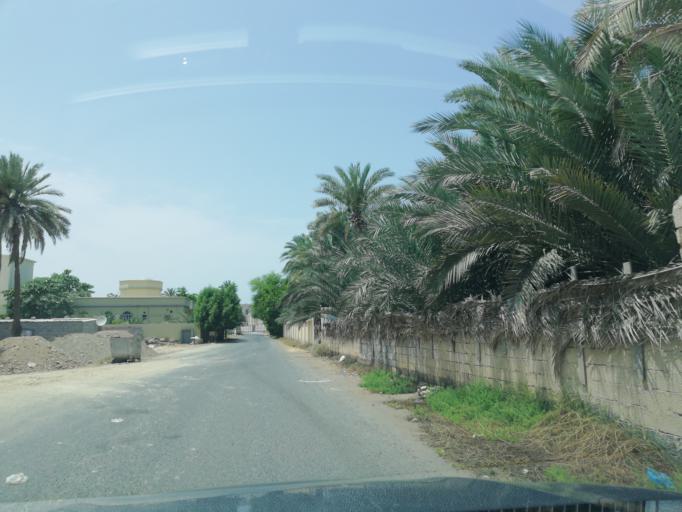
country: OM
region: Muhafazat Masqat
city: As Sib al Jadidah
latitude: 23.6583
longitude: 58.2127
